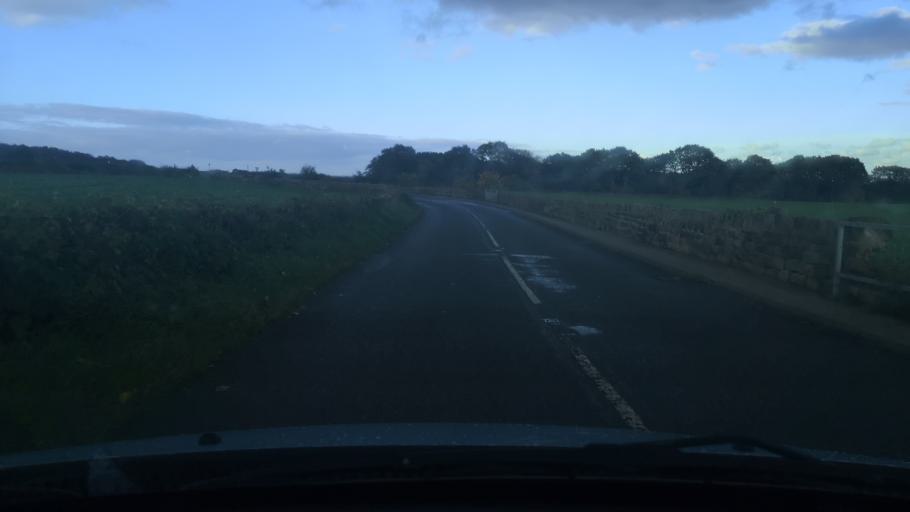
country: GB
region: England
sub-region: City and Borough of Wakefield
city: Woolley
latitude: 53.6190
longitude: -1.5174
